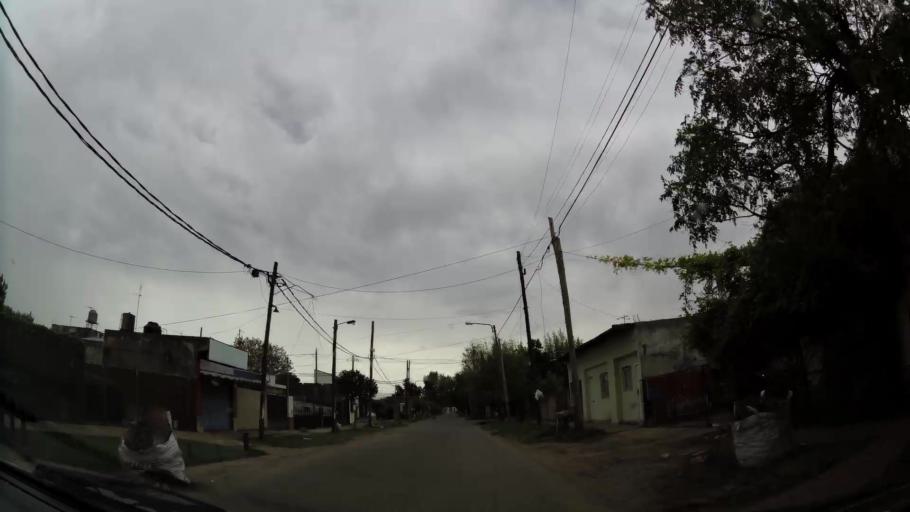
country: AR
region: Buenos Aires
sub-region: Partido de Quilmes
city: Quilmes
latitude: -34.7963
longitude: -58.2695
